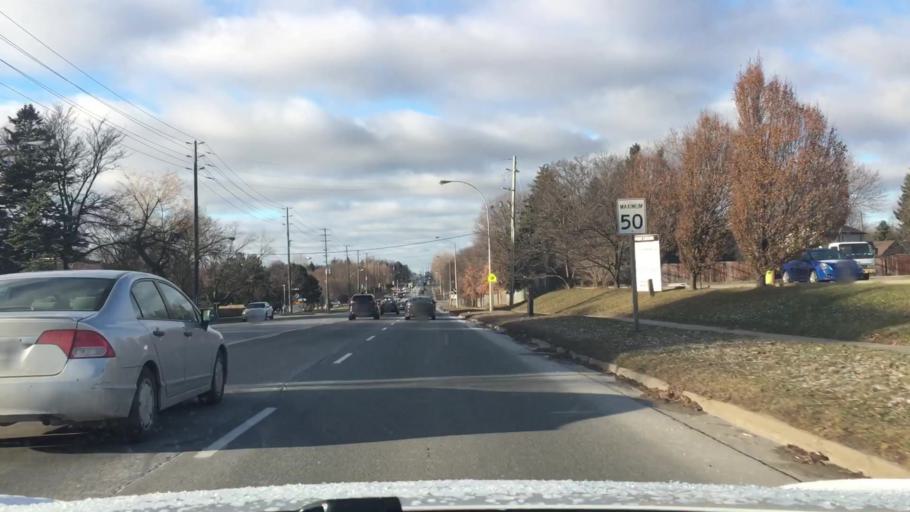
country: CA
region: Ontario
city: Markham
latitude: 43.8711
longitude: -79.2690
